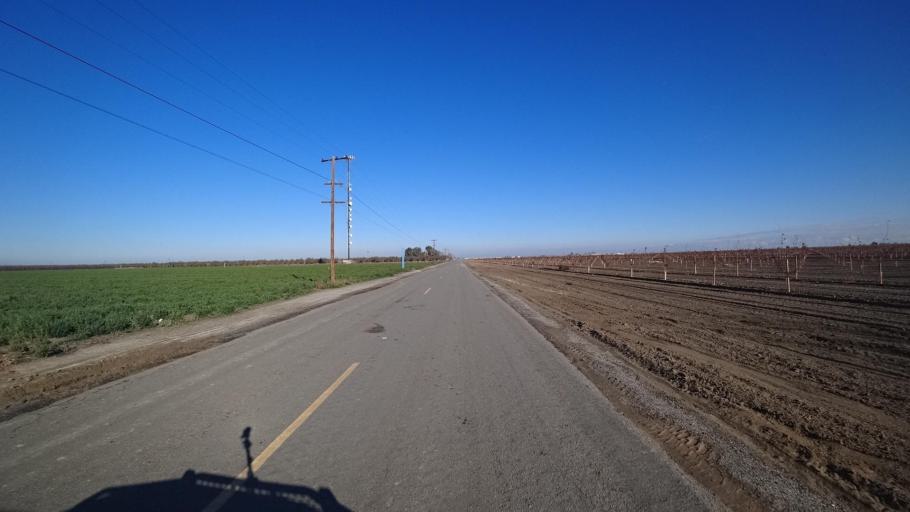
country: US
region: California
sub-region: Kern County
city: Delano
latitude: 35.7507
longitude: -119.3119
